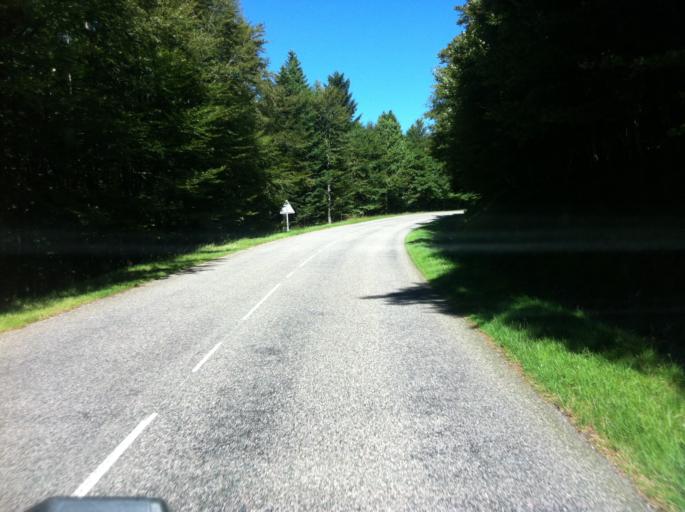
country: FR
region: Alsace
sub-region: Departement du Haut-Rhin
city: Metzeral
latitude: 48.0694
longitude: 7.0214
